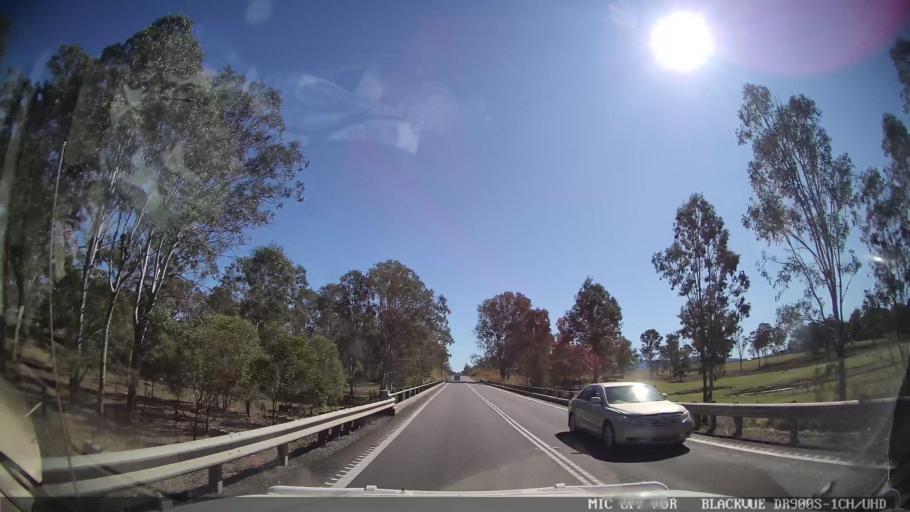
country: AU
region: Queensland
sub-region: Gympie Regional Council
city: Gympie
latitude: -26.0399
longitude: 152.5703
